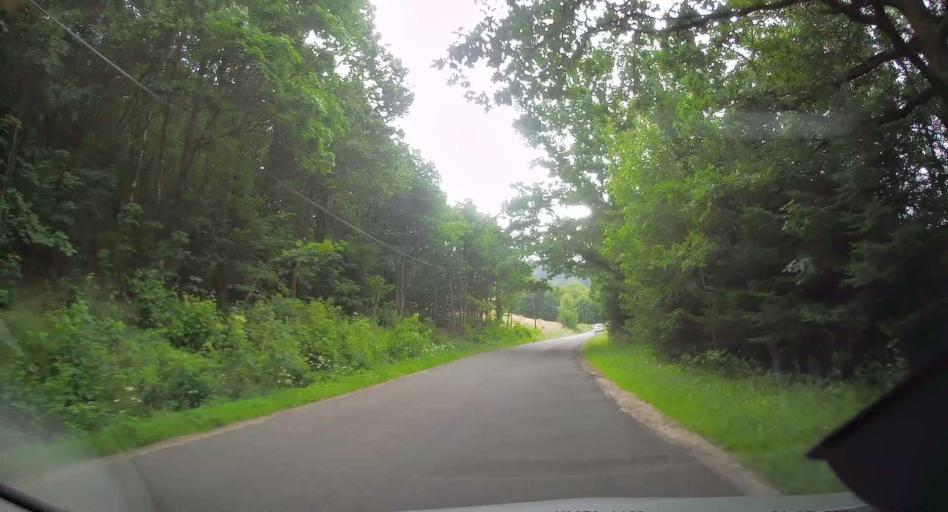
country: PL
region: Lower Silesian Voivodeship
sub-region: Powiat kamiennogorski
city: Marciszow
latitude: 50.8426
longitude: 15.9816
